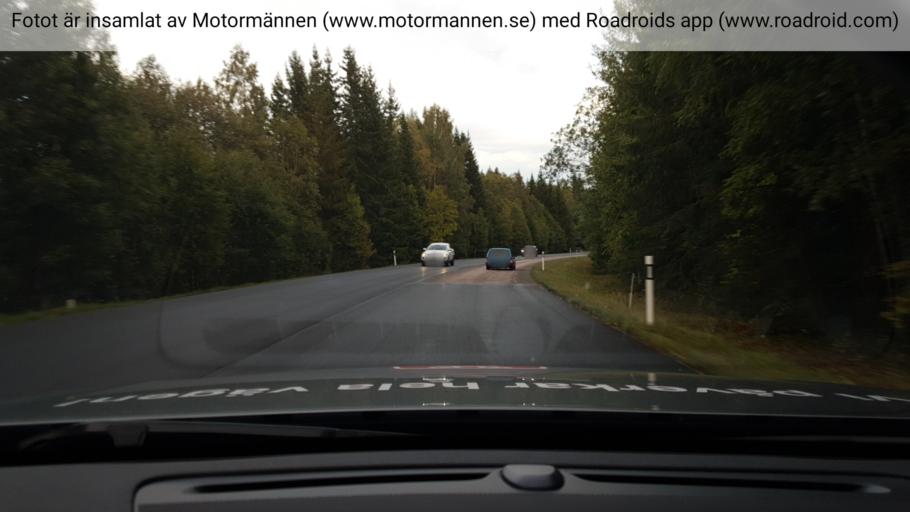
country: SE
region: Vaestra Goetaland
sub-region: Amals Kommun
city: Amal
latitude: 59.0528
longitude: 12.4861
